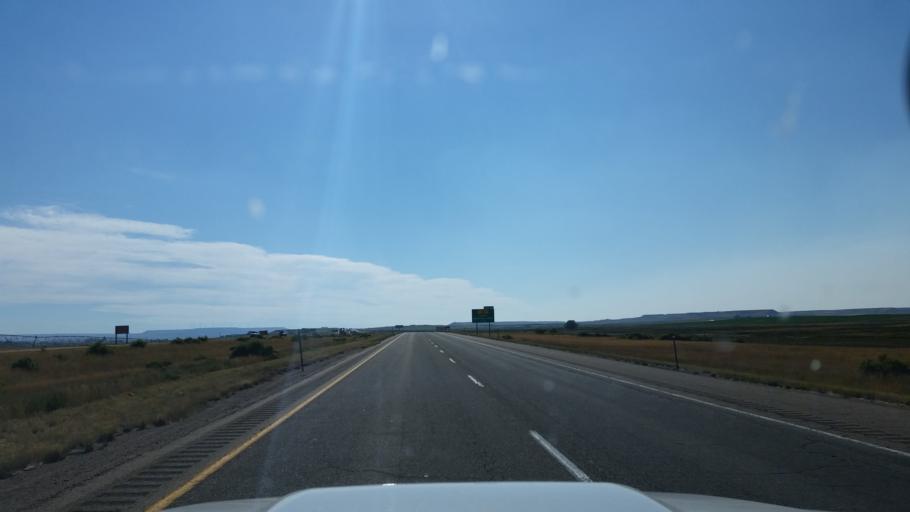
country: US
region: Wyoming
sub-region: Uinta County
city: Lyman
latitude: 41.3643
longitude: -110.3125
